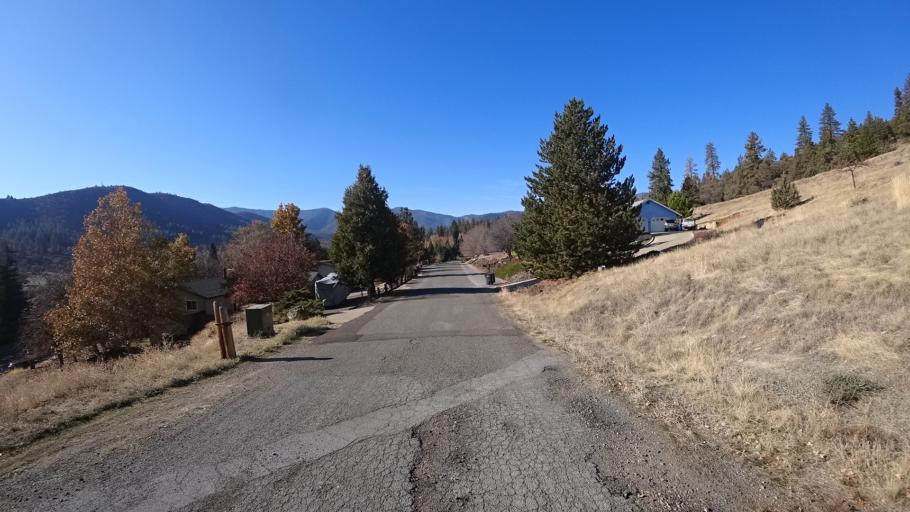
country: US
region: California
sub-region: Siskiyou County
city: Yreka
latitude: 41.6938
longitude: -122.6521
